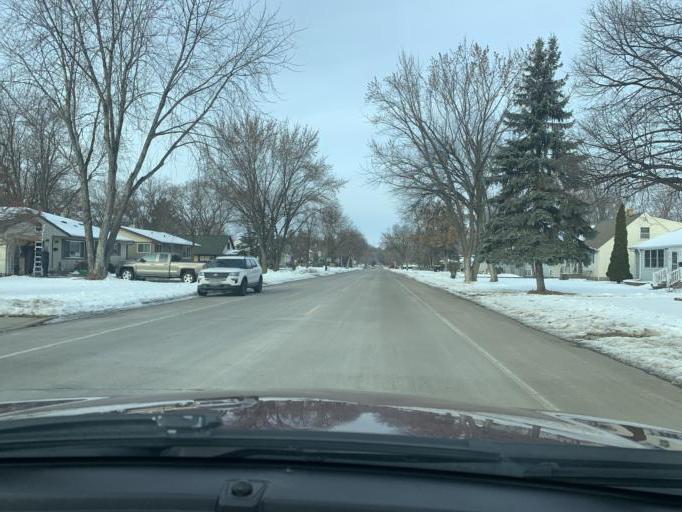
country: US
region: Minnesota
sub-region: Washington County
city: Saint Paul Park
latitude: 44.8350
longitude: -92.9841
